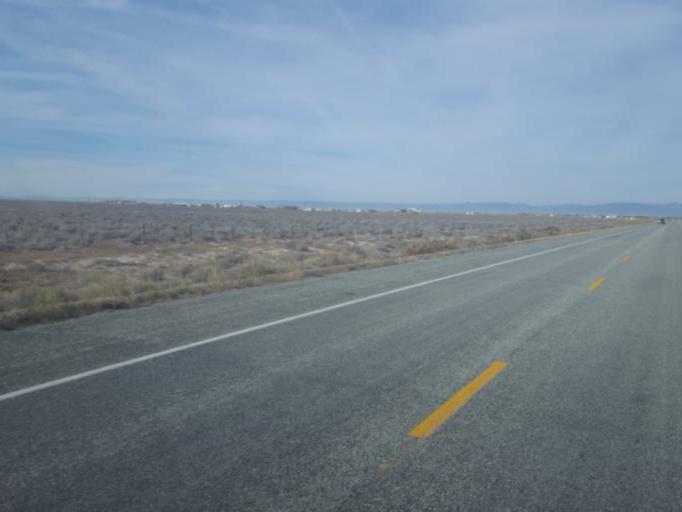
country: US
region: Colorado
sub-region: Alamosa County
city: Alamosa East
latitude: 37.4748
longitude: -105.6671
